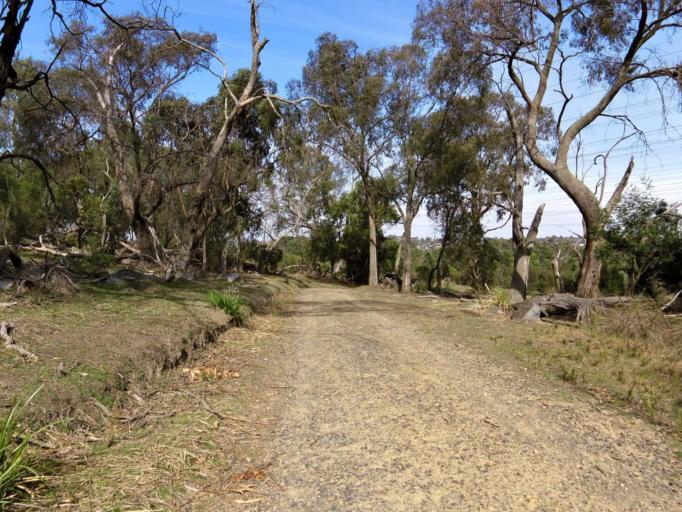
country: AU
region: Victoria
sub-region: Casey
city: Endeavour Hills
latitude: -37.9548
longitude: 145.2627
